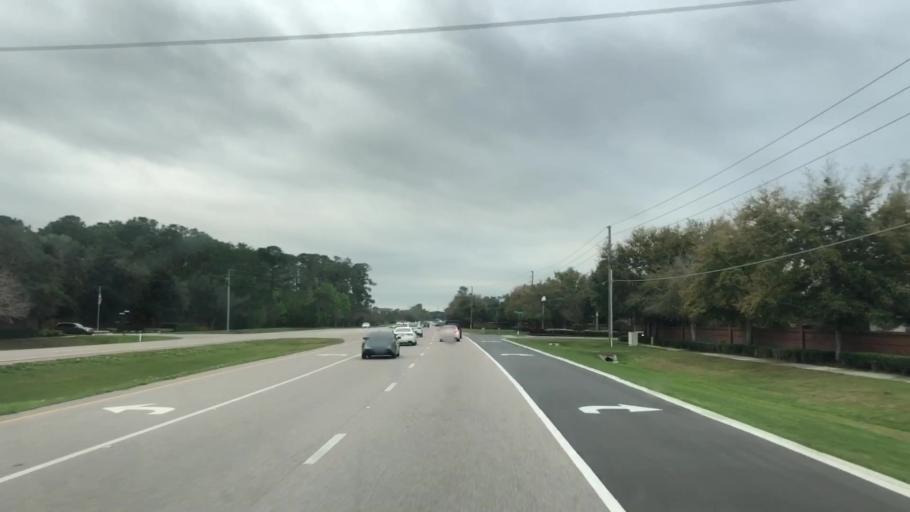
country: US
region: Florida
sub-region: Orange County
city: Bay Hill
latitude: 28.4246
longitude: -81.5331
